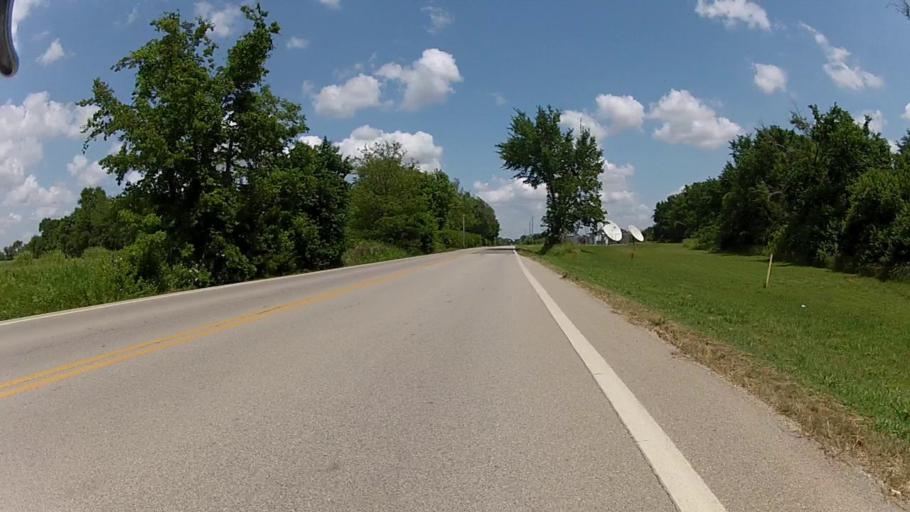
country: US
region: Kansas
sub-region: Labette County
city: Altamont
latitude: 37.1930
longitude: -95.3100
